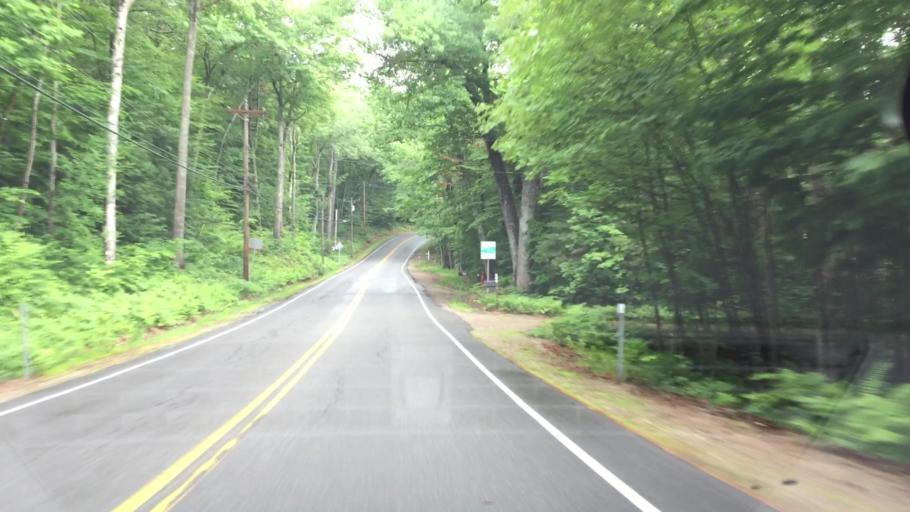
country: US
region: New Hampshire
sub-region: Carroll County
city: Center Harbor
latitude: 43.7335
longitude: -71.4761
